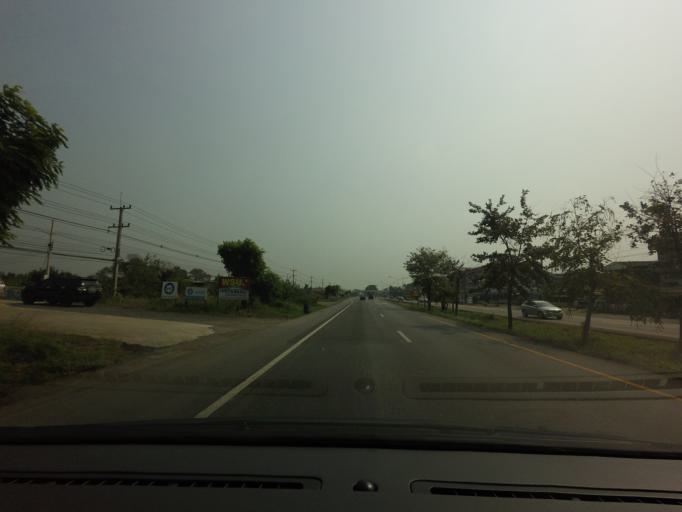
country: TH
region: Prachuap Khiri Khan
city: Kui Buri
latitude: 12.0844
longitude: 99.8556
